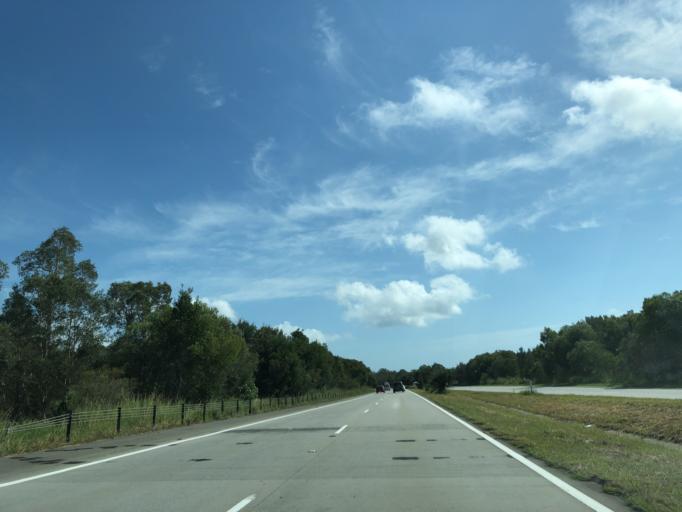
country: AU
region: New South Wales
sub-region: Byron Shire
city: Brunswick Heads
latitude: -28.5670
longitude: 153.5411
